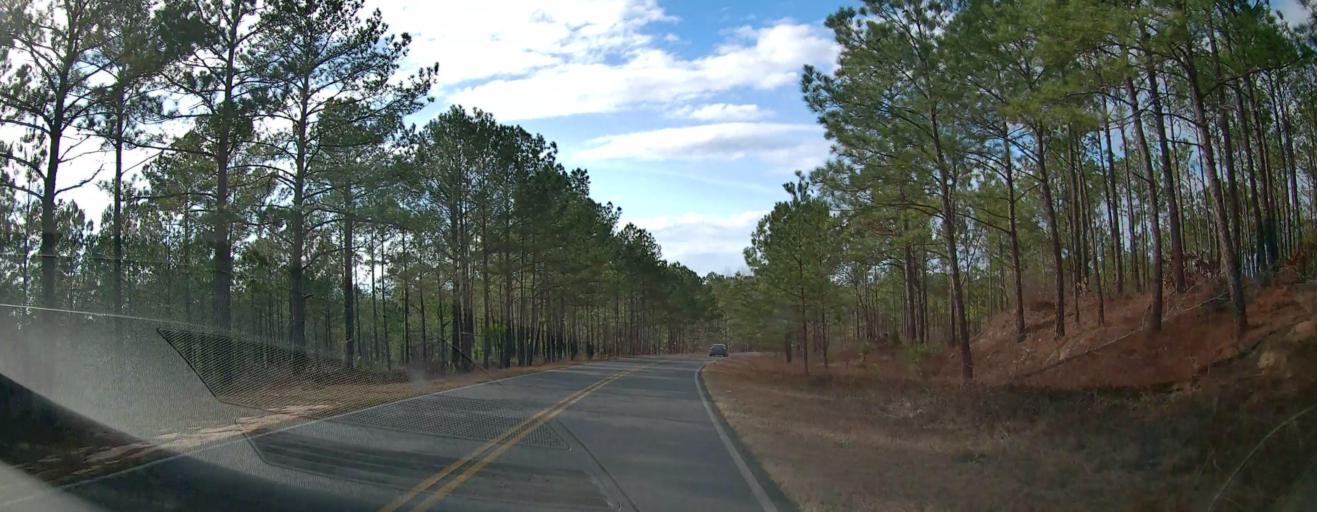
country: US
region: Georgia
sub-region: Talbot County
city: Talbotton
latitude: 32.4982
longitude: -84.5792
